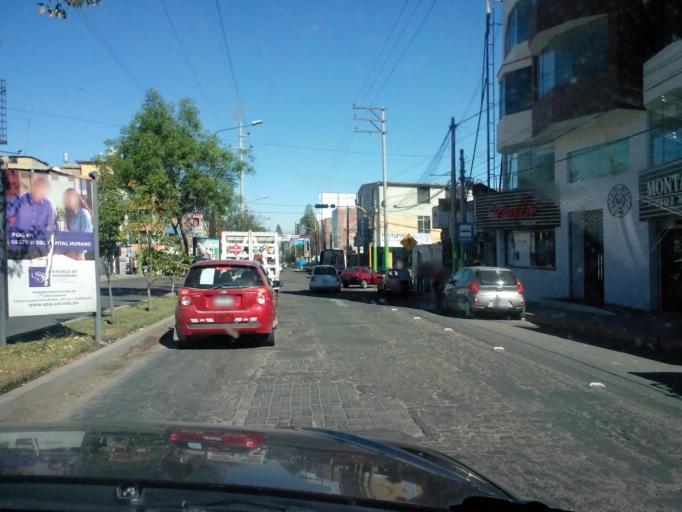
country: PE
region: Arequipa
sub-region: Provincia de Arequipa
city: Arequipa
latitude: -16.3794
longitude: -71.5569
